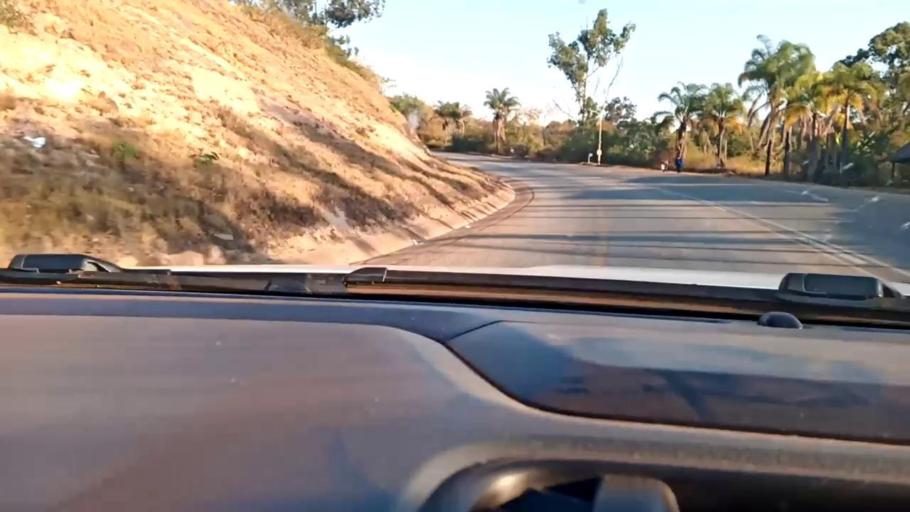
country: ZA
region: Limpopo
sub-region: Mopani District Municipality
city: Duiwelskloof
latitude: -23.6899
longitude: 30.1467
